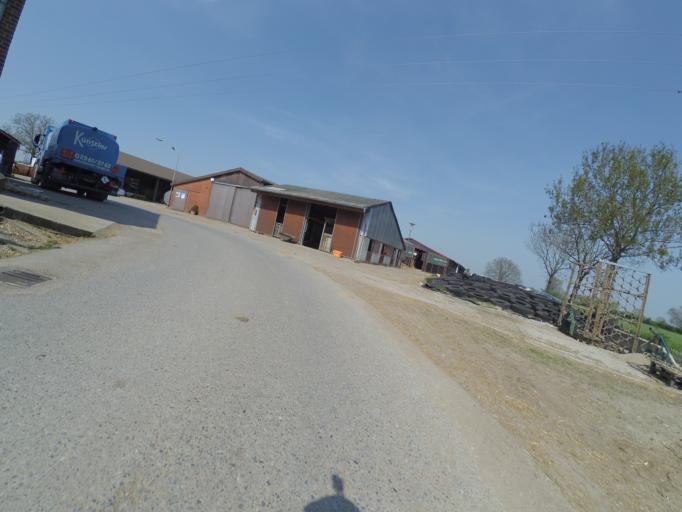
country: NL
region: Gelderland
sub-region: Oude IJsselstreek
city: Gendringen
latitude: 51.8383
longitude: 6.3359
